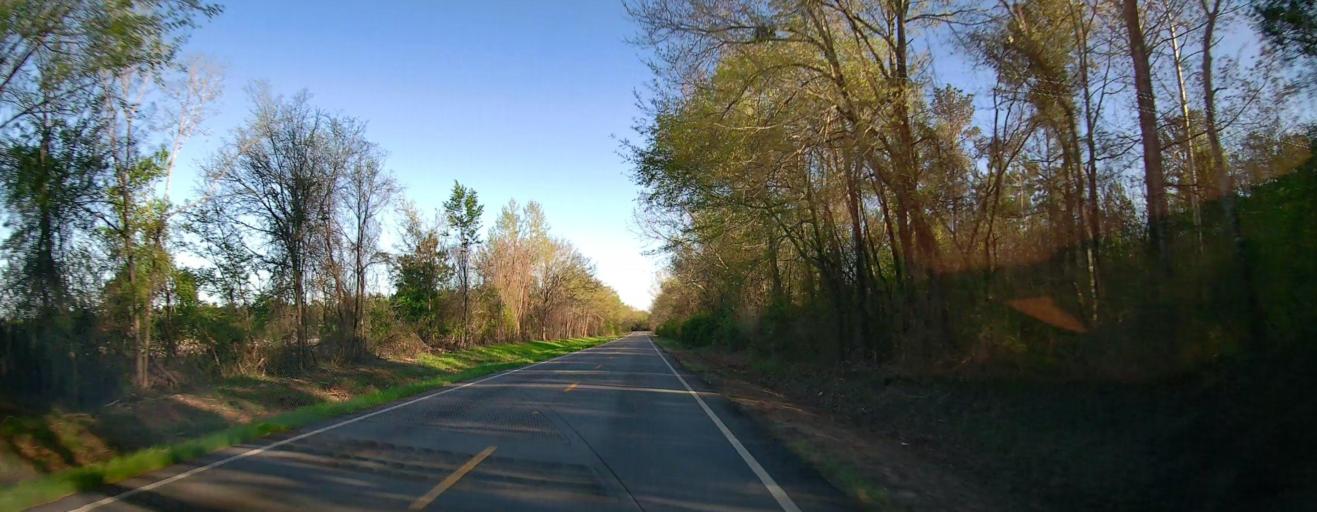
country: US
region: Georgia
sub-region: Baldwin County
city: Hardwick
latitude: 32.9596
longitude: -83.1693
